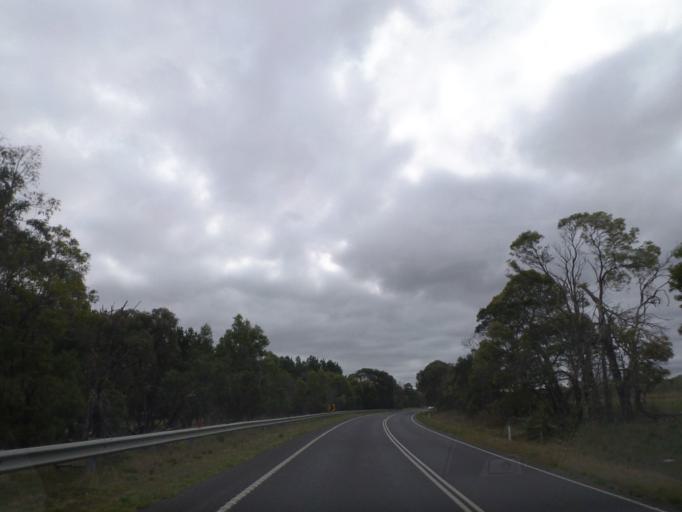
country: AU
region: Victoria
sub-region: Whittlesea
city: Whittlesea
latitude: -37.4087
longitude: 145.0197
